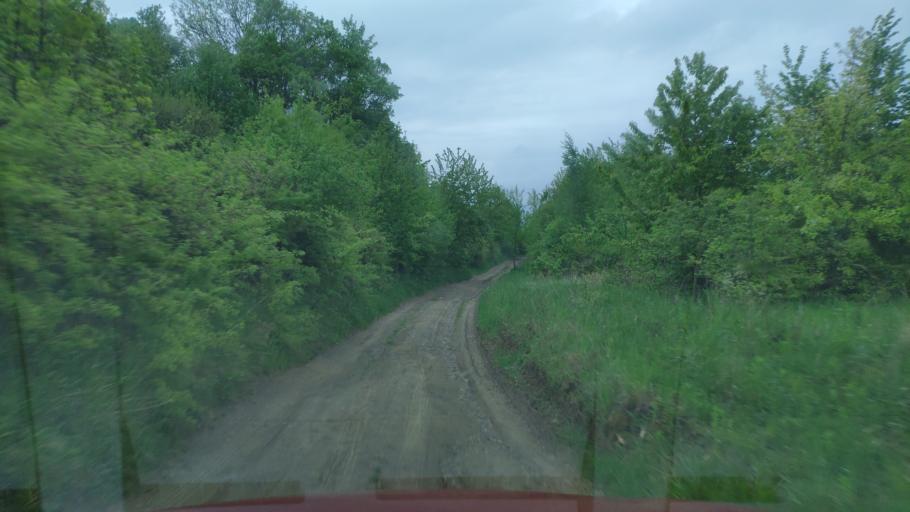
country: SK
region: Kosicky
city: Kosice
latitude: 48.7676
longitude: 21.2080
